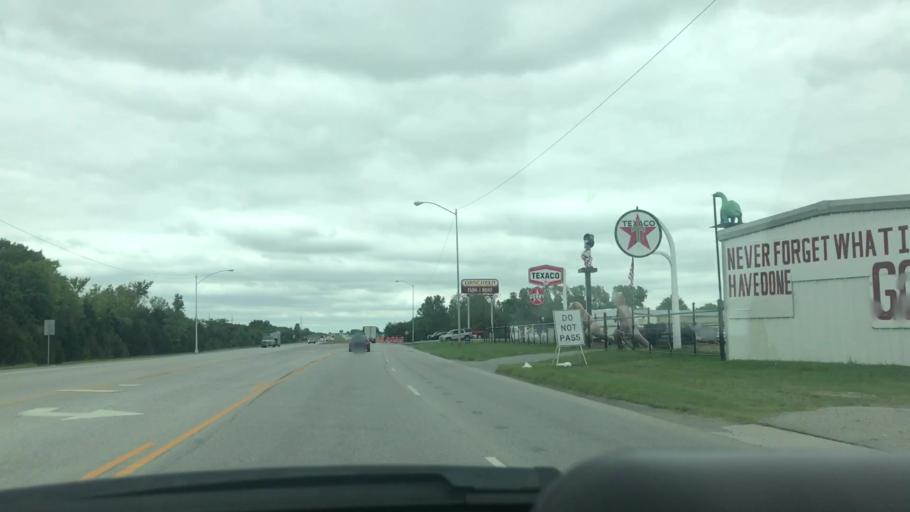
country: US
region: Oklahoma
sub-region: Mayes County
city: Pryor
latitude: 36.3166
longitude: -95.3156
